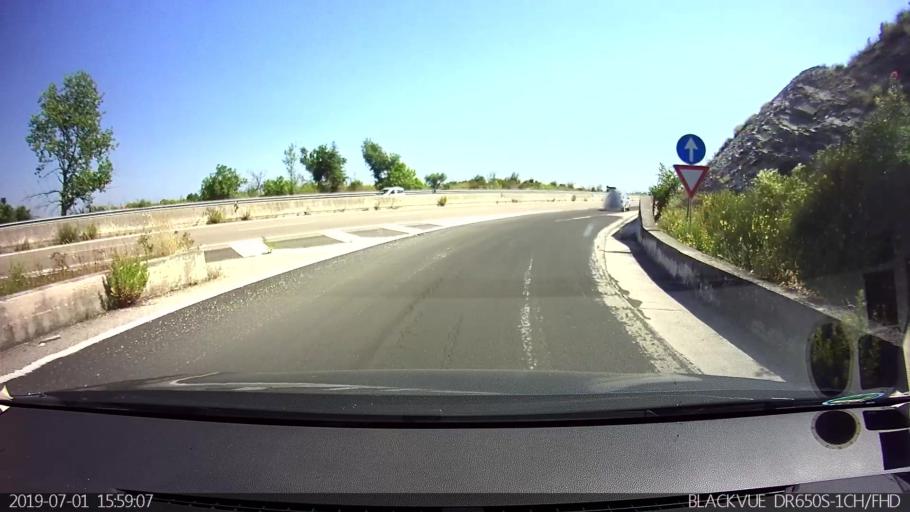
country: IT
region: Latium
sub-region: Provincia di Frosinone
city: Sant'Angelo in Villa-Giglio
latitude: 41.6633
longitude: 13.4247
